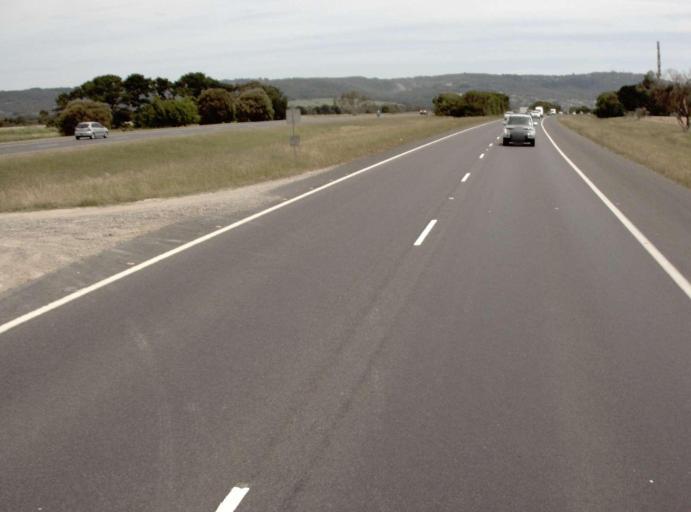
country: AU
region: Victoria
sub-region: Mornington Peninsula
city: Safety Beach
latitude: -38.3183
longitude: 145.0102
